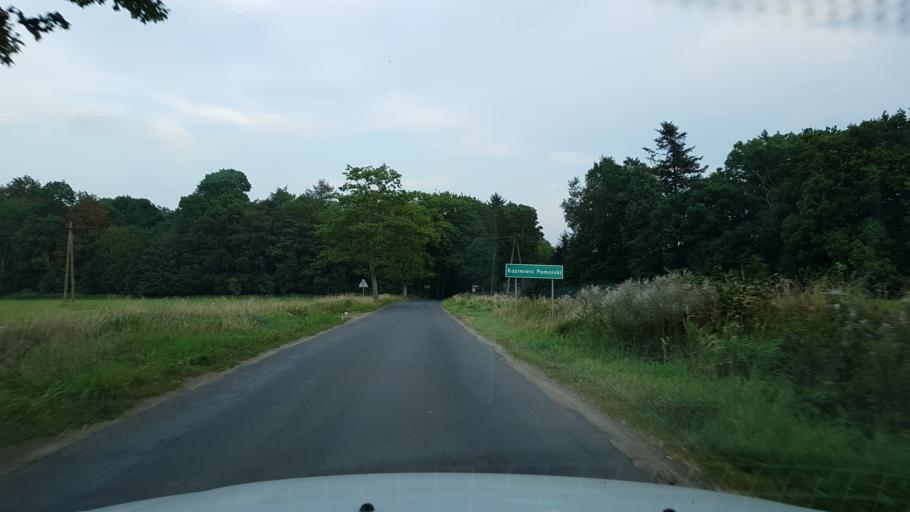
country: PL
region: West Pomeranian Voivodeship
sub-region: Powiat koszalinski
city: Mielno
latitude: 54.2287
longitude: 16.0218
